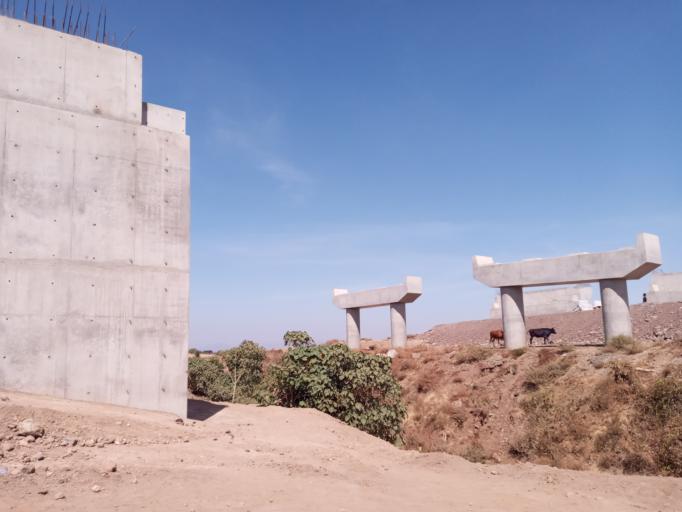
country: ET
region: Oromiya
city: Shashemene
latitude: 7.3664
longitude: 38.6445
